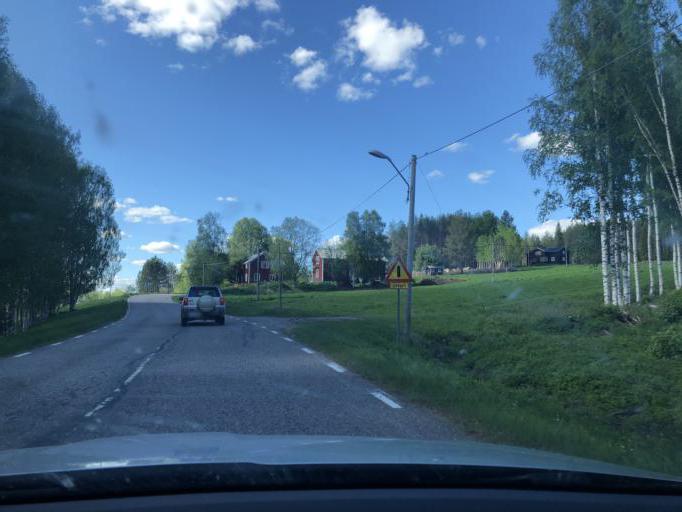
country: SE
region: Norrbotten
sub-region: Kalix Kommun
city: Kalix
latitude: 65.9983
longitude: 23.1446
